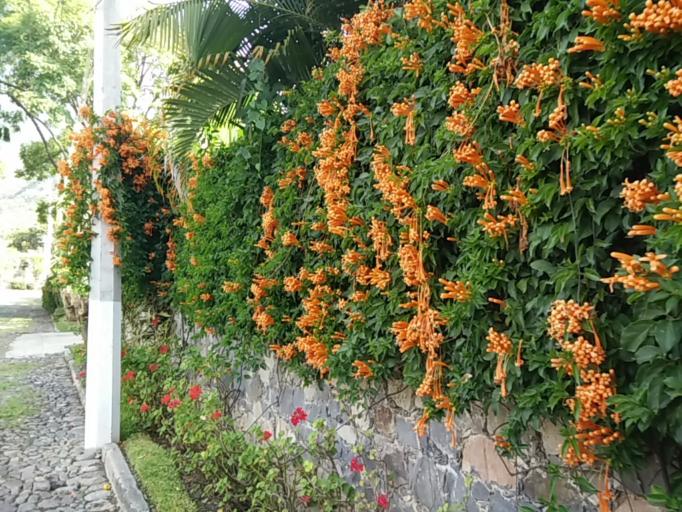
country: MX
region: Jalisco
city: Ajijic
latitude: 20.2983
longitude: -103.2738
